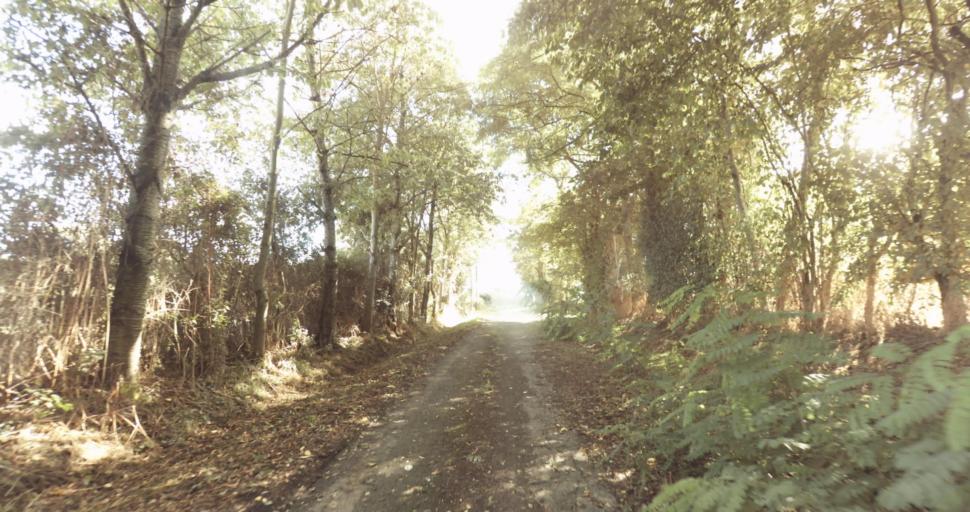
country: FR
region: Lower Normandy
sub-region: Departement de l'Orne
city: Vimoutiers
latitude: 48.9315
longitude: 0.1352
